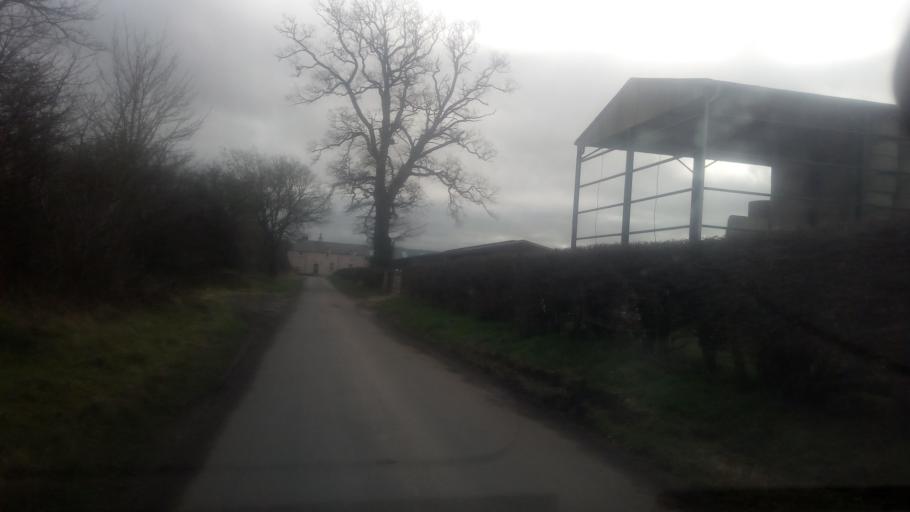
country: GB
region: Scotland
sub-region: The Scottish Borders
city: Kelso
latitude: 55.5440
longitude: -2.4716
